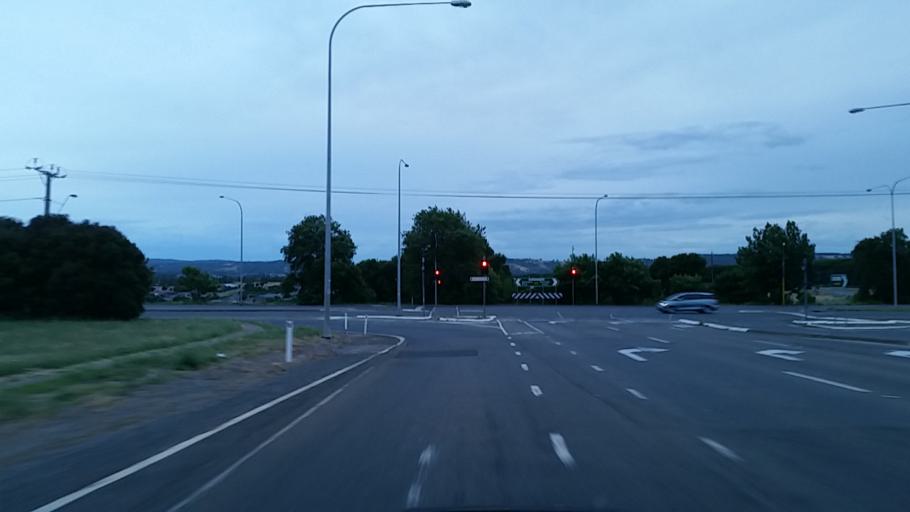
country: AU
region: South Australia
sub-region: Onkaparinga
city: Bedford Park
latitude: -35.0537
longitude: 138.5587
